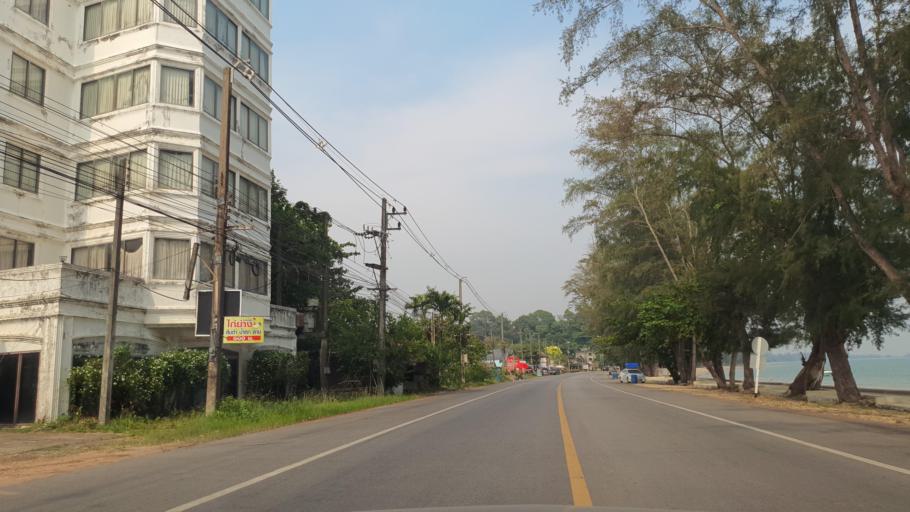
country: TH
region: Rayong
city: Rayong
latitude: 12.6305
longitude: 101.4479
